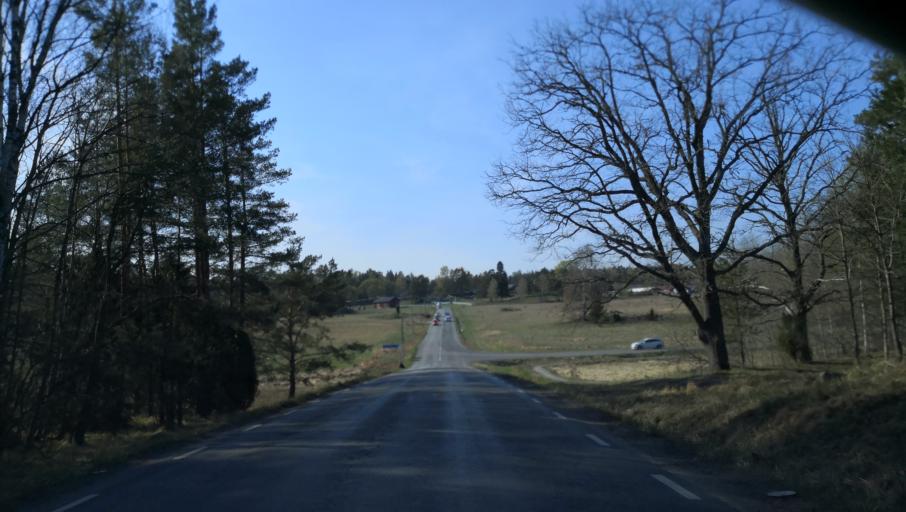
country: SE
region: Stockholm
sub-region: Varmdo Kommun
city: Hemmesta
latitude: 59.3242
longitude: 18.5484
